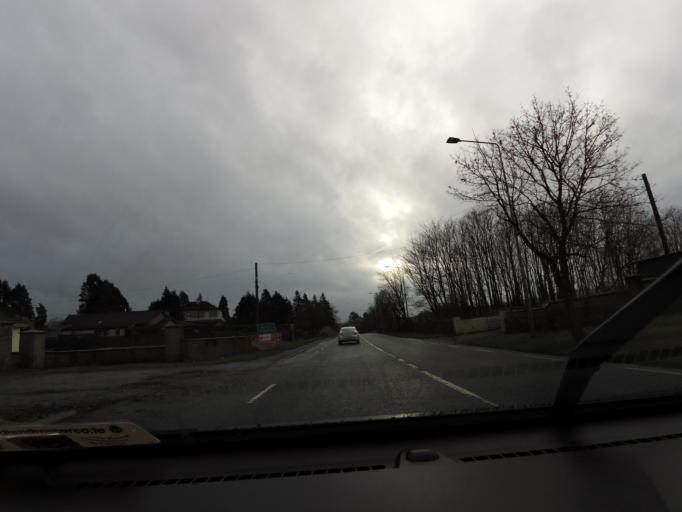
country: IE
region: Munster
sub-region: North Tipperary
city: Roscrea
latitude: 52.9616
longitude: -7.8063
